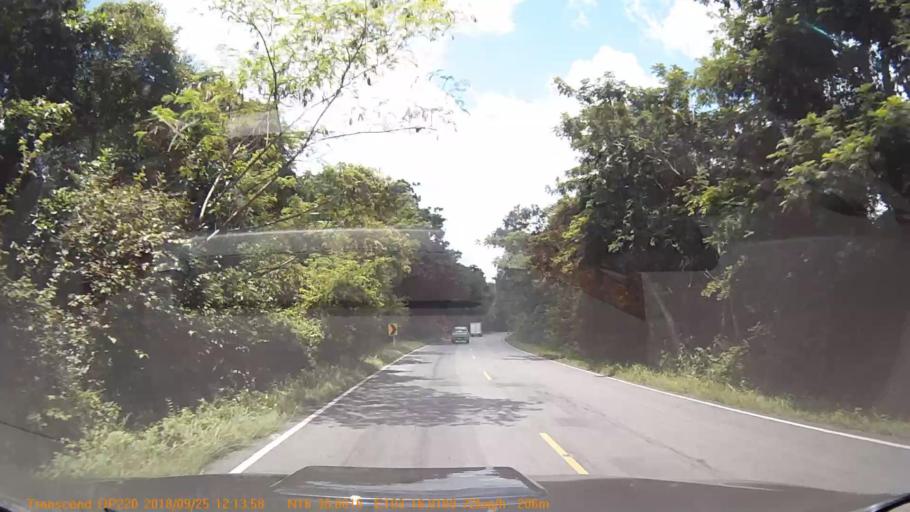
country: TH
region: Kalasin
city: Huai Mek
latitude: 16.5101
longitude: 103.2669
